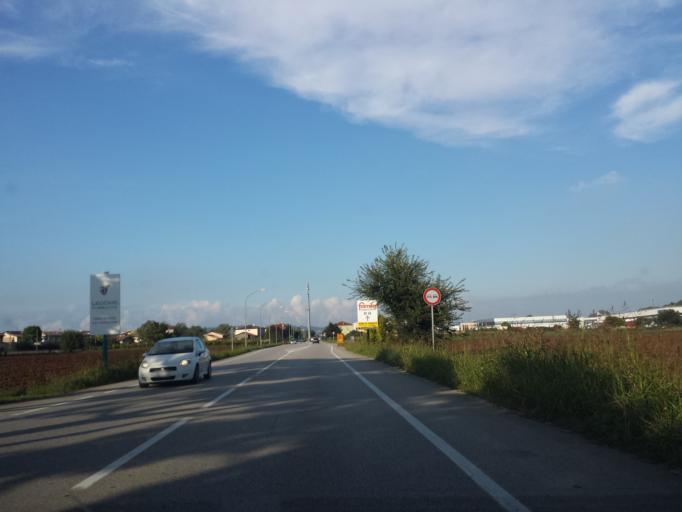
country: IT
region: Veneto
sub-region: Provincia di Vicenza
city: Brendola
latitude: 45.4927
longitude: 11.4403
